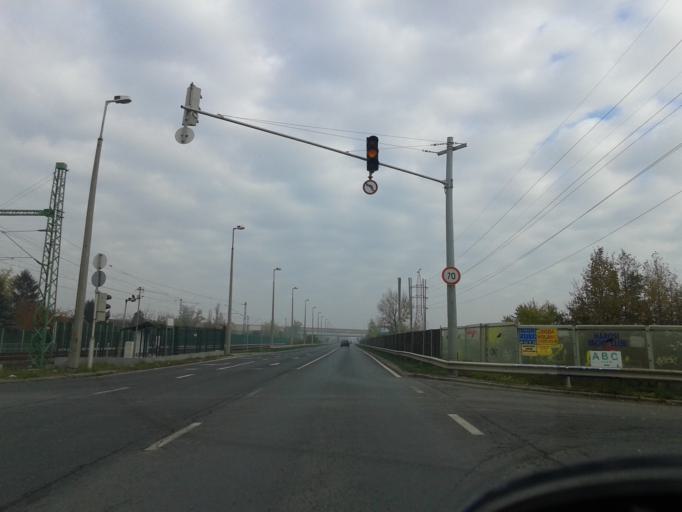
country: HU
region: Pest
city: Halasztelek
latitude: 47.3965
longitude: 19.0032
